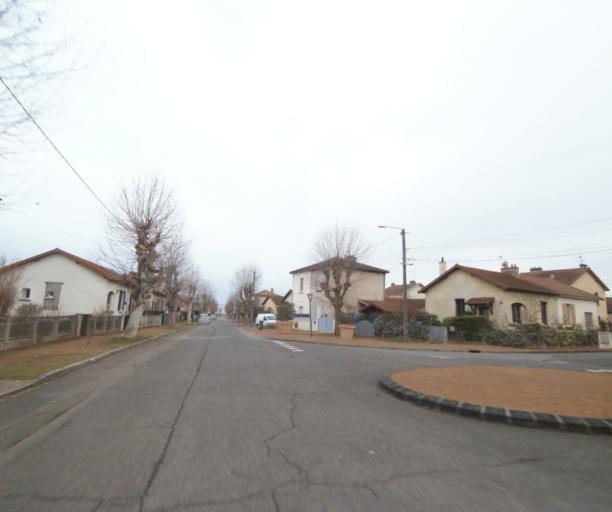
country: FR
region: Rhone-Alpes
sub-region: Departement de la Loire
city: Le Coteau
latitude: 46.0542
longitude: 4.0890
